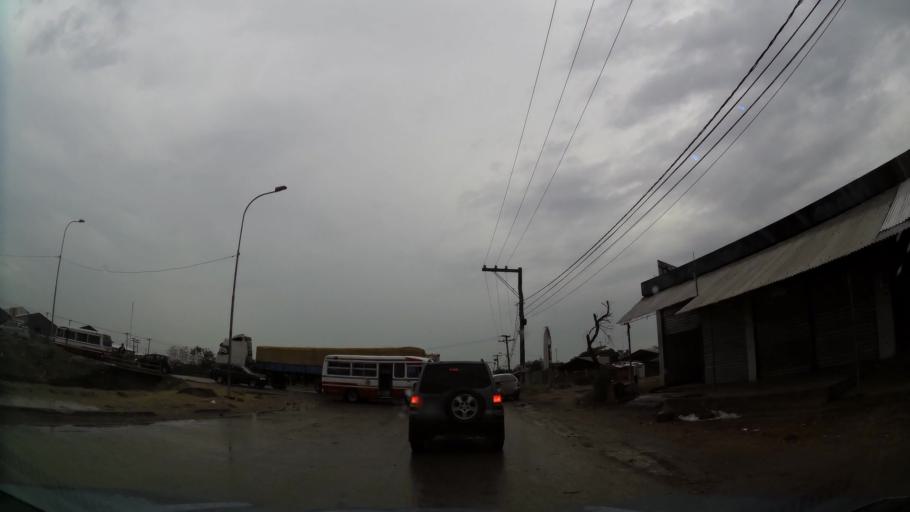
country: BO
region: Santa Cruz
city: Santa Cruz de la Sierra
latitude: -17.7553
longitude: -63.1308
